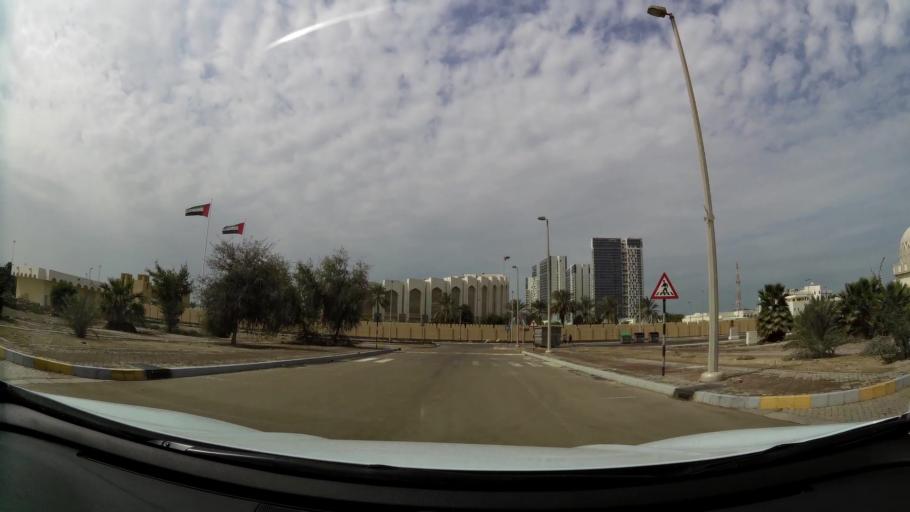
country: AE
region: Abu Dhabi
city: Abu Dhabi
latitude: 24.4113
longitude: 54.4682
